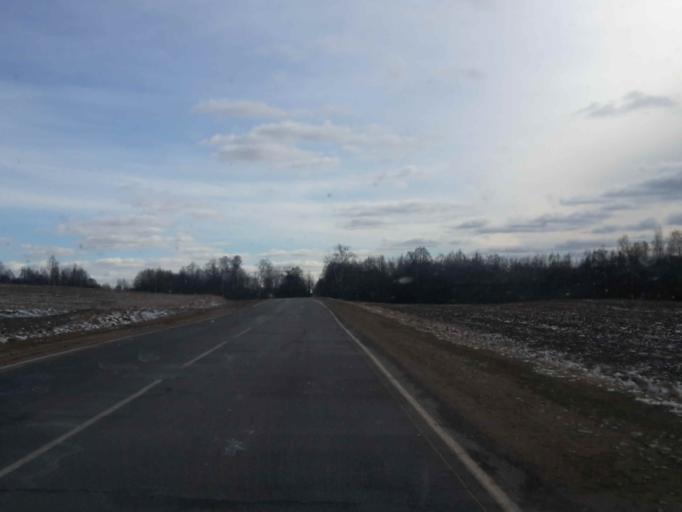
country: BY
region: Minsk
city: Myadzyel
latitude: 54.9907
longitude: 26.8865
